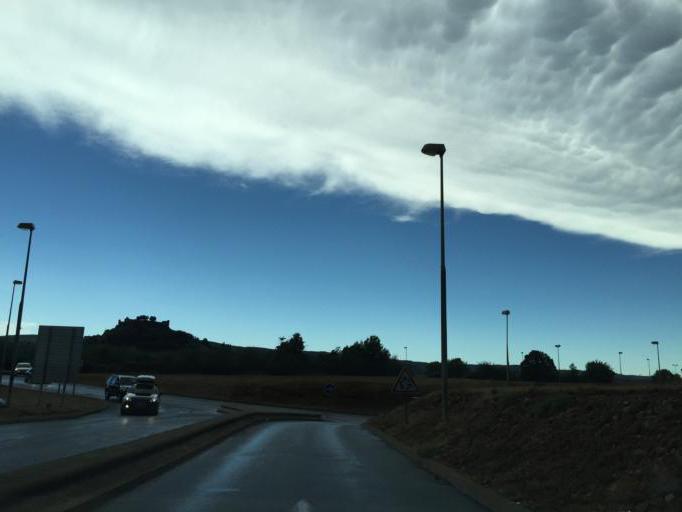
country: FR
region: Midi-Pyrenees
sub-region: Departement de l'Aveyron
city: Severac-le-Chateau
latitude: 44.3312
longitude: 3.0799
